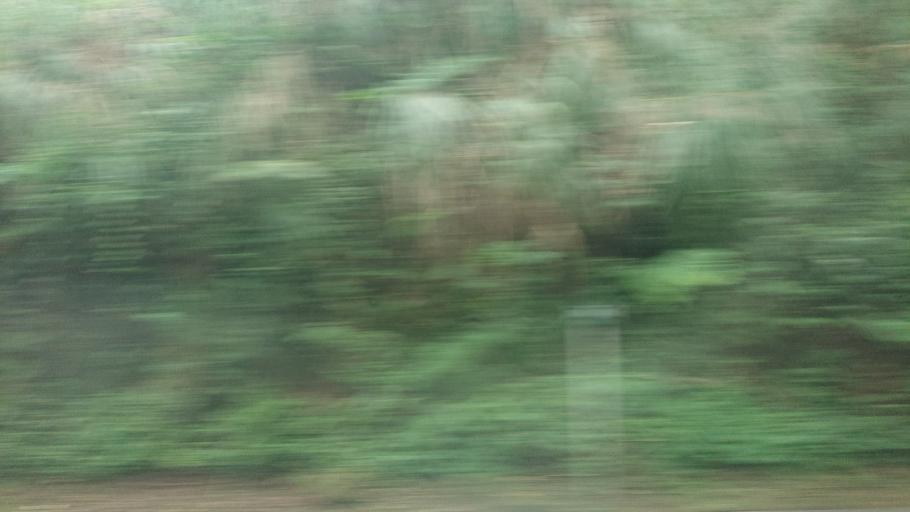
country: TW
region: Taiwan
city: Lugu
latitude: 23.4924
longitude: 120.7927
